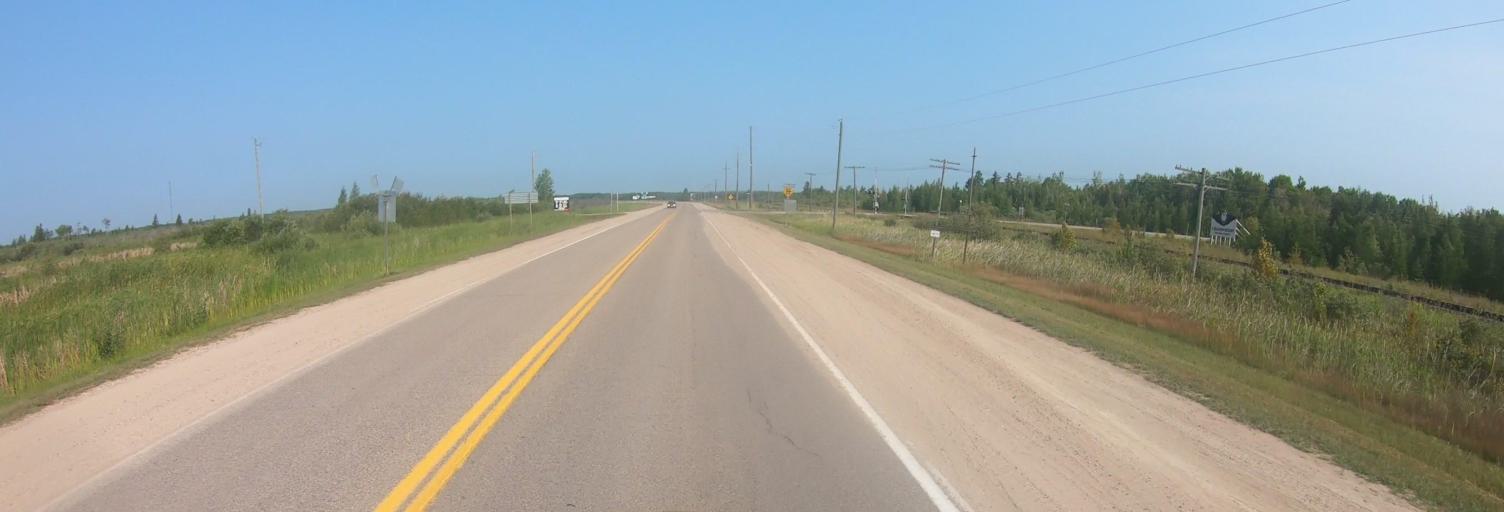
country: US
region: Minnesota
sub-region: Roseau County
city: Warroad
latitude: 49.0014
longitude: -95.3780
